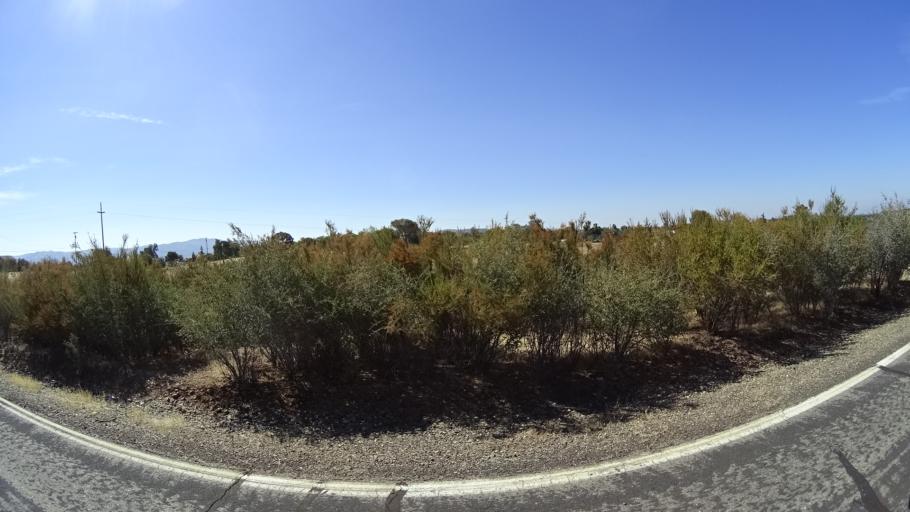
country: US
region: California
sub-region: Calaveras County
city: Rancho Calaveras
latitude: 38.1650
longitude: -120.8639
